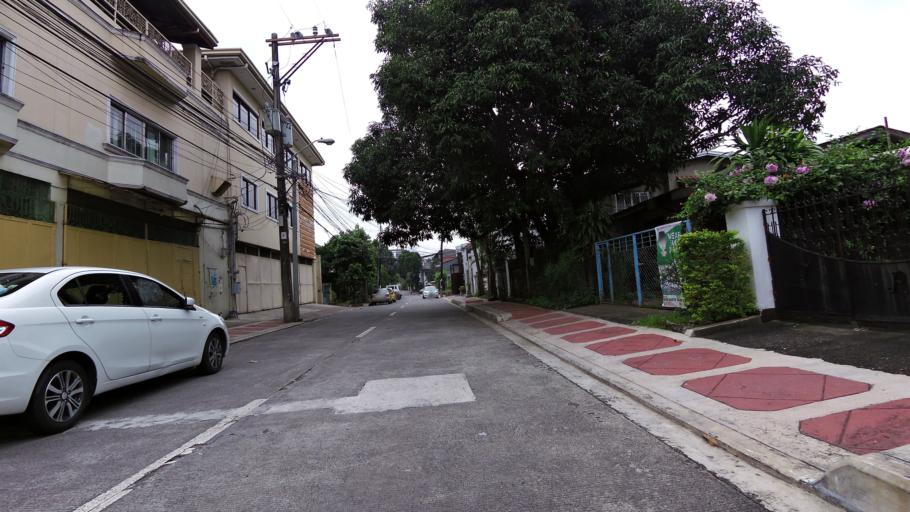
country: PH
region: Metro Manila
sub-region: Quezon City
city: Quezon City
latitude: 14.6444
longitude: 121.0571
